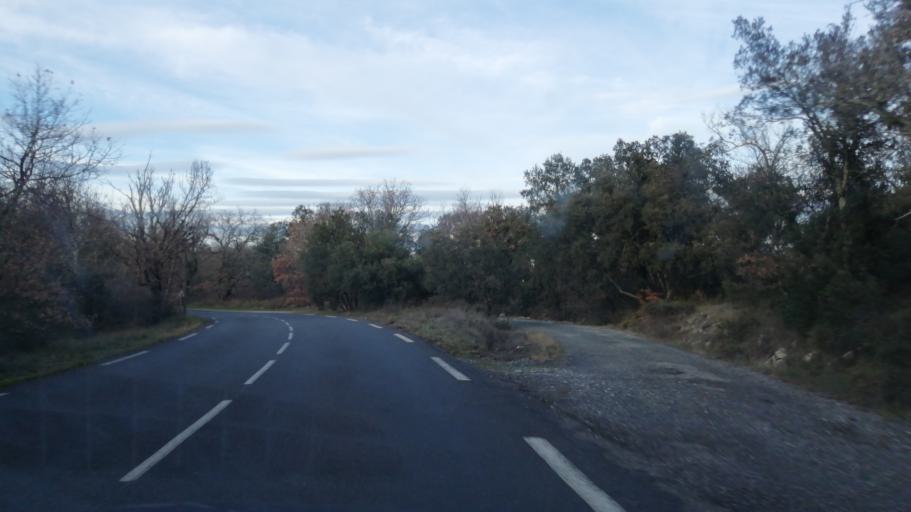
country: FR
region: Languedoc-Roussillon
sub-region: Departement de l'Herault
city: Claret
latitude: 43.8352
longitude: 3.9224
